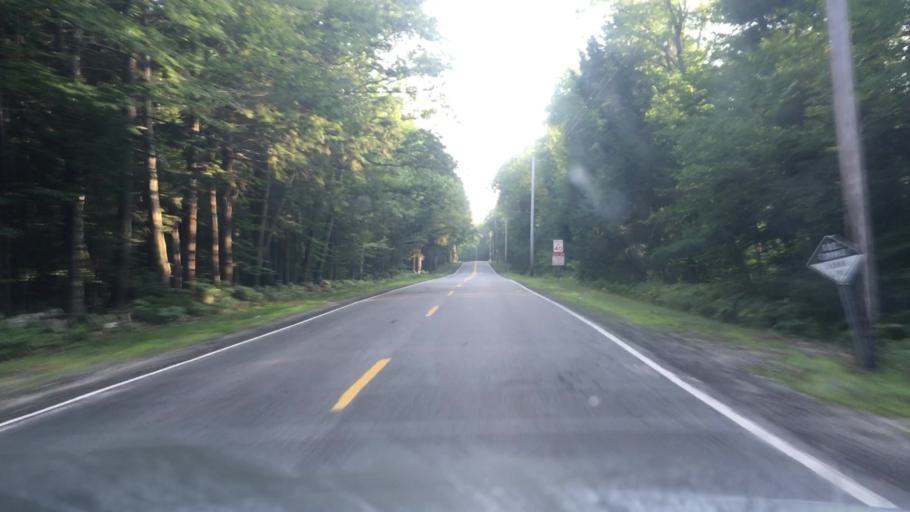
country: US
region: Maine
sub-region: Androscoggin County
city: Lisbon Falls
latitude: 43.9289
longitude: -70.0866
